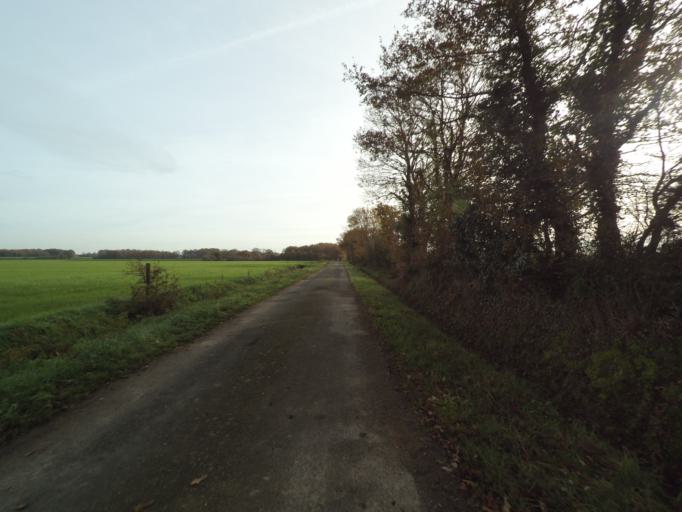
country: FR
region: Pays de la Loire
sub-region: Departement de la Loire-Atlantique
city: La Planche
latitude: 47.0097
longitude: -1.4062
